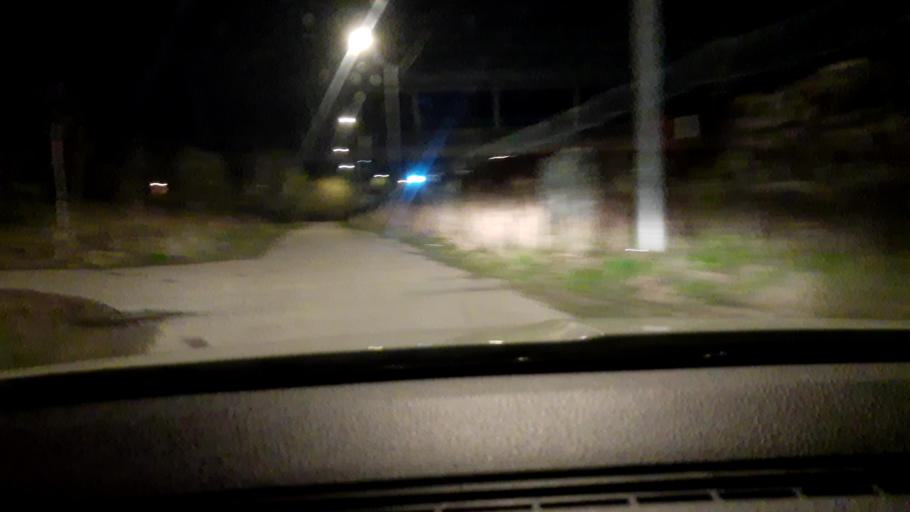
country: RU
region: Moskovskaya
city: Annino
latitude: 55.6198
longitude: 37.2587
